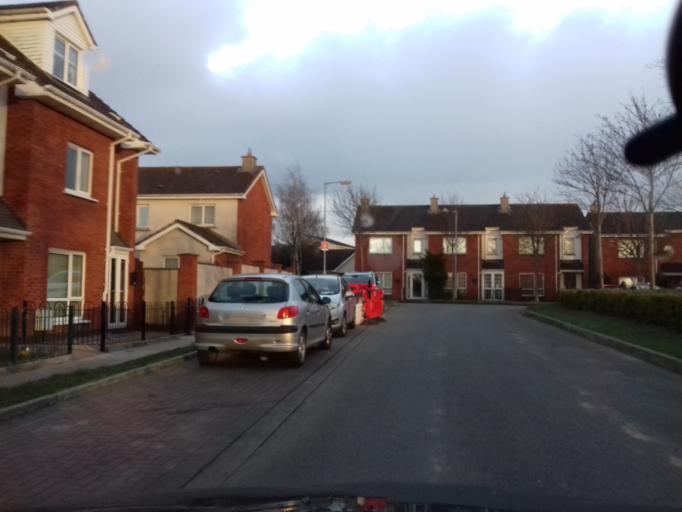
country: IE
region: Leinster
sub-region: Fingal County
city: Blanchardstown
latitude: 53.4033
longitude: -6.3914
